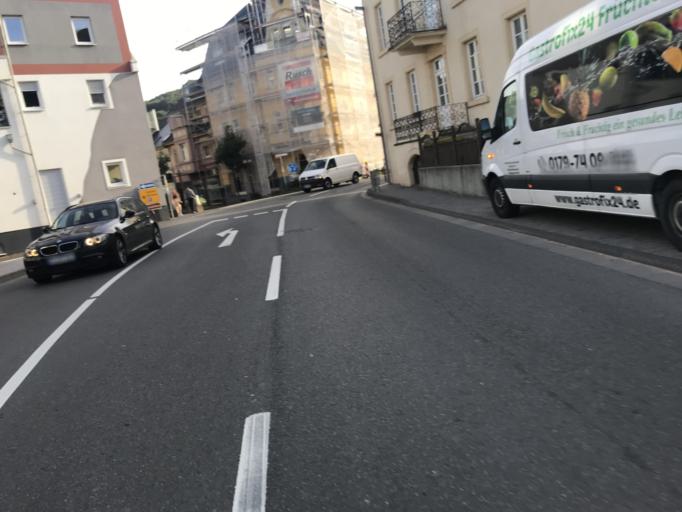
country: DE
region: Rheinland-Pfalz
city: Kirn
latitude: 49.7884
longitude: 7.4573
